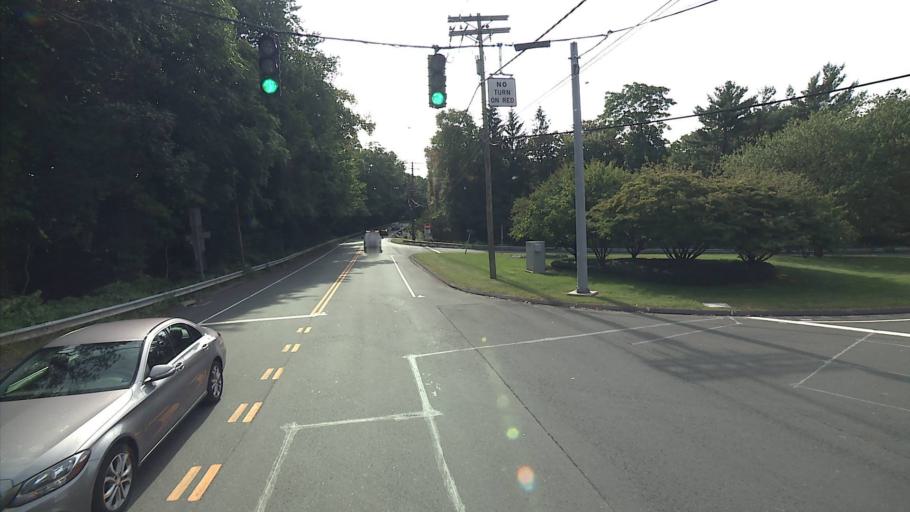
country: US
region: Connecticut
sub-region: Fairfield County
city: New Canaan
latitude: 41.1487
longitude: -73.4827
